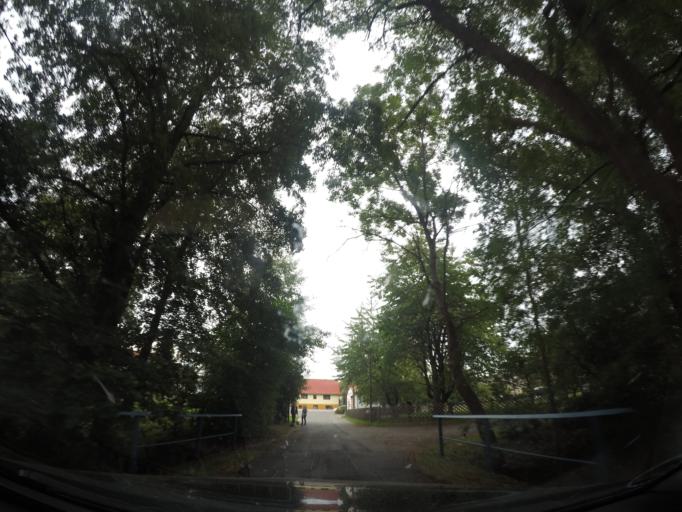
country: DE
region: Thuringia
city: Drogen
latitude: 50.8909
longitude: 12.3250
